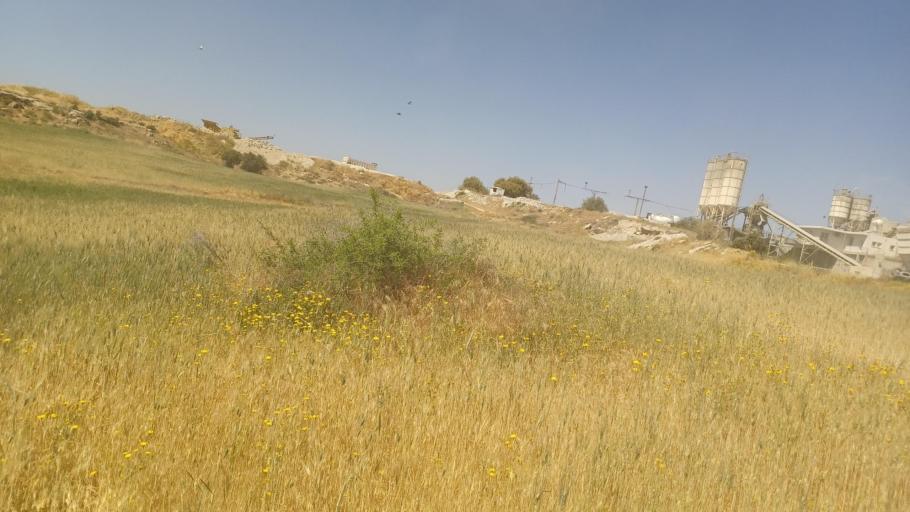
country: CY
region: Lefkosia
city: Kokkinotrimithia
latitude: 35.1546
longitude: 33.2384
